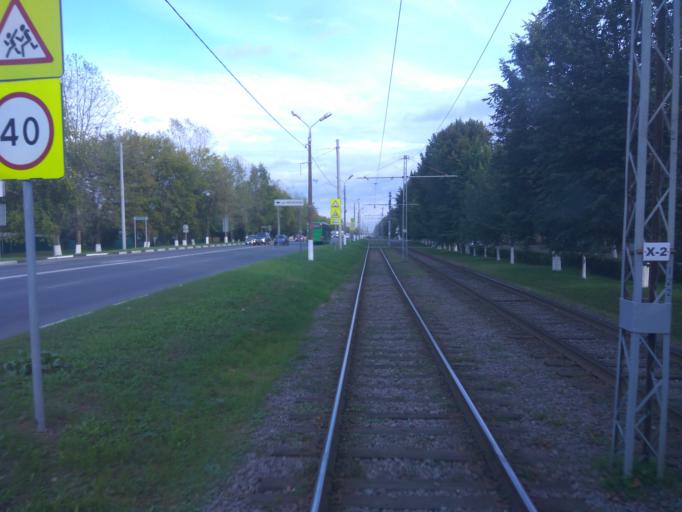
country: RU
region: Moskovskaya
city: Kolomna
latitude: 55.0900
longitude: 38.7824
